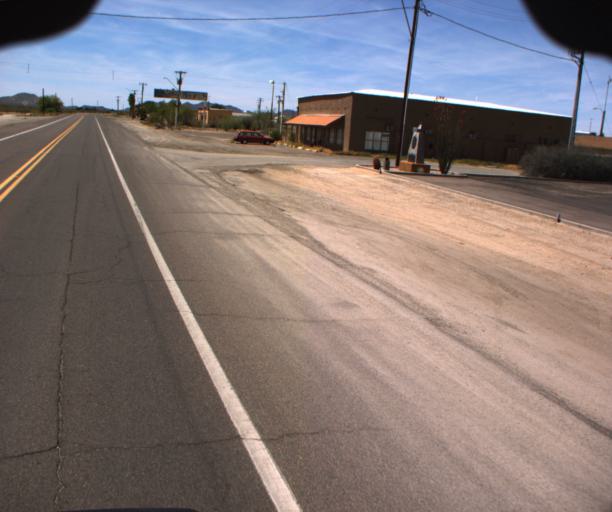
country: US
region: Arizona
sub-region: La Paz County
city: Salome
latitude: 33.7808
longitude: -113.6152
